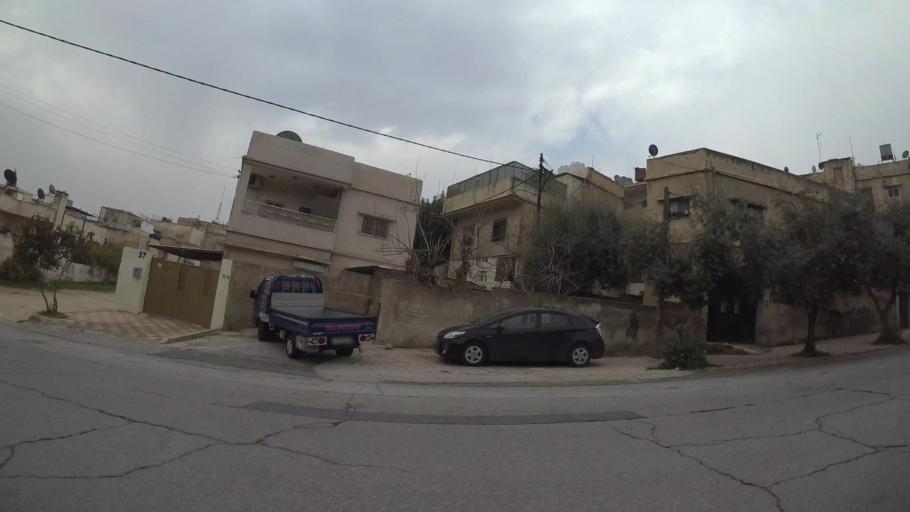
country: JO
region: Amman
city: Amman
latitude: 31.9588
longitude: 35.9438
